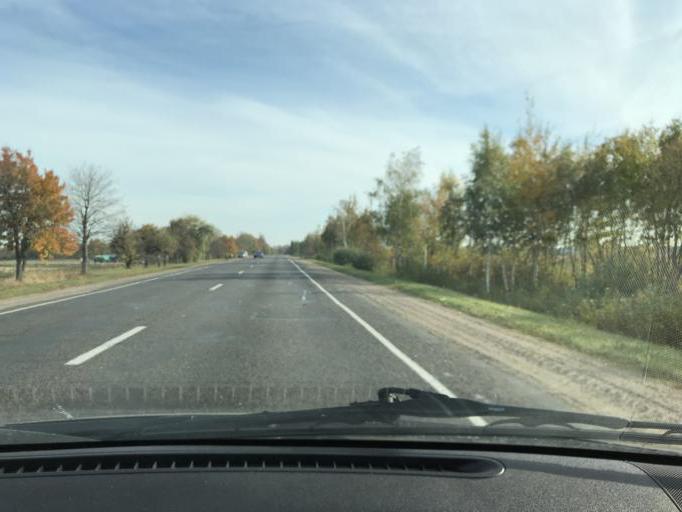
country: BY
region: Brest
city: Asnyezhytsy
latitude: 52.2041
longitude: 26.0578
